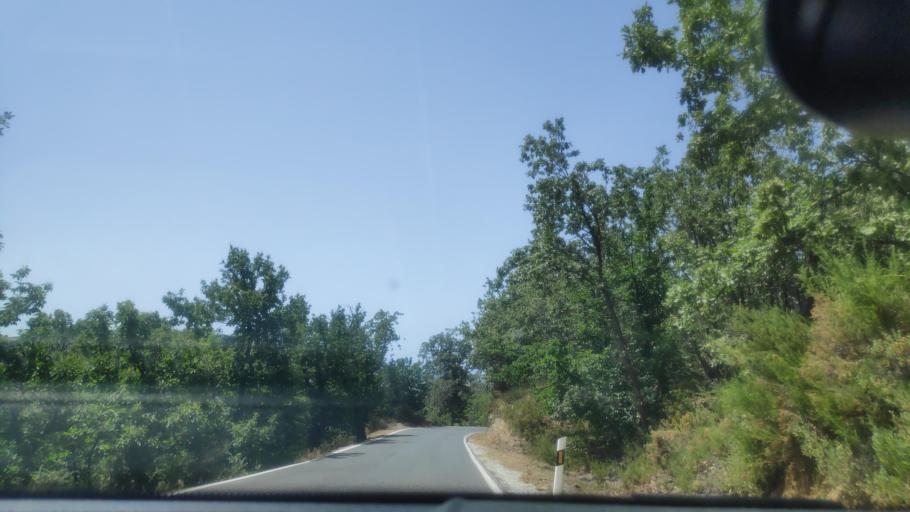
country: ES
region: Andalusia
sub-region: Provincia de Granada
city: Busquistar
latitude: 36.9541
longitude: -3.2788
